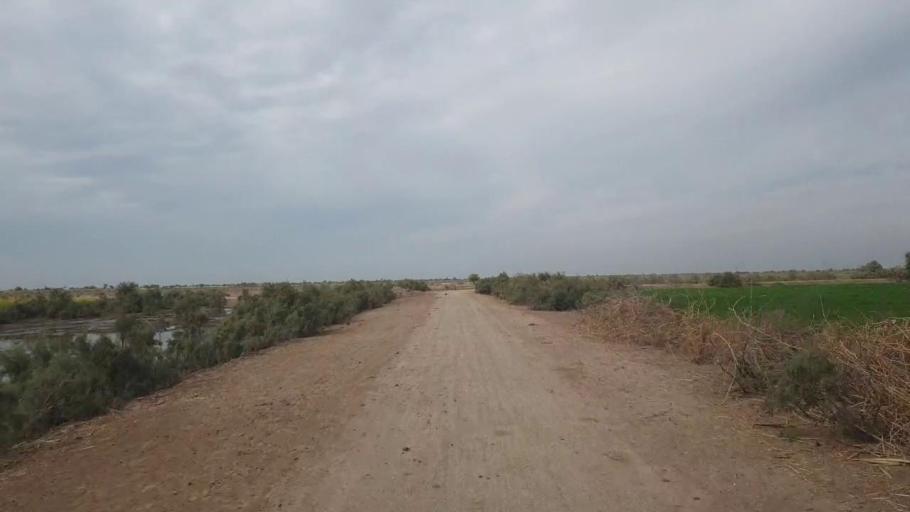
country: PK
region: Sindh
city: Sanghar
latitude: 26.0478
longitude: 68.9052
